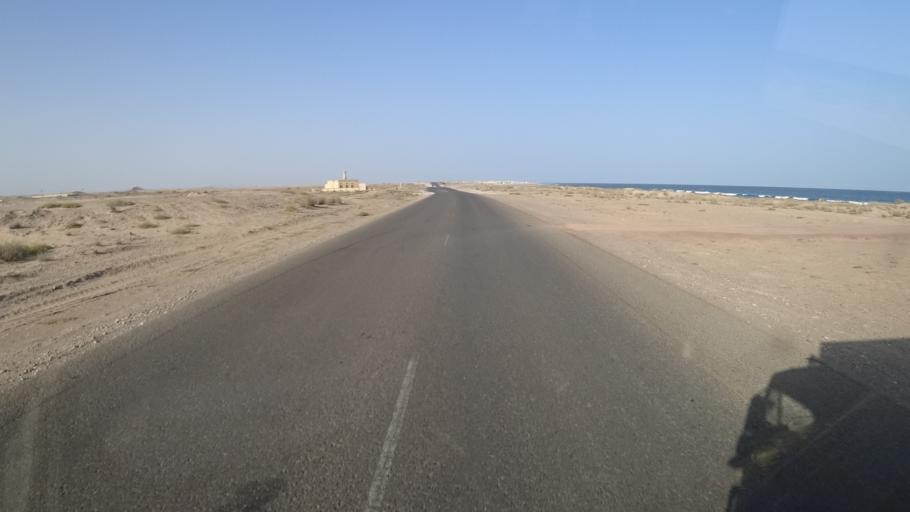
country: OM
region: Ash Sharqiyah
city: Sur
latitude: 22.1474
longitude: 59.7353
